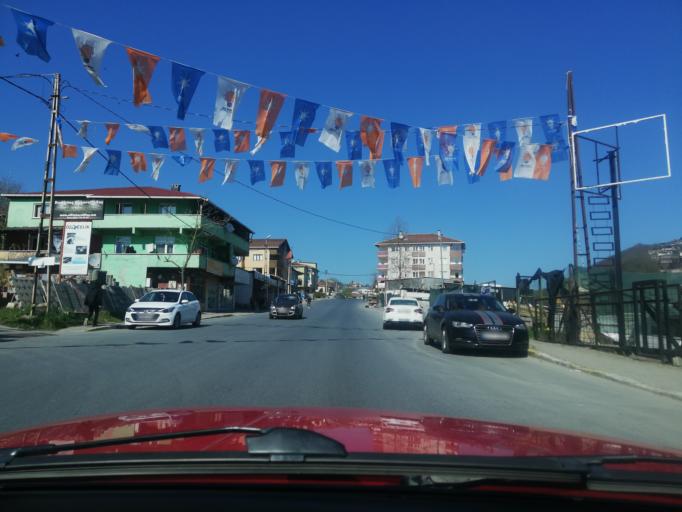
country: TR
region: Istanbul
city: Mahmut Sevket Pasa
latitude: 41.0927
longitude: 29.1423
